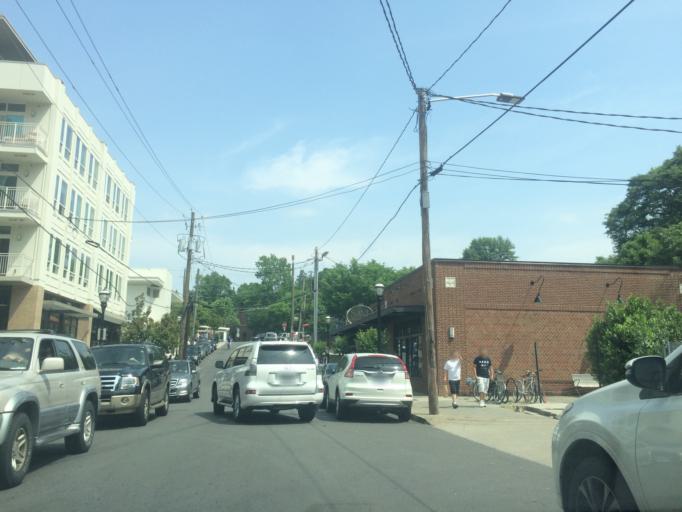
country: US
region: Georgia
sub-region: DeKalb County
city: Druid Hills
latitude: 33.7620
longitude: -84.3579
